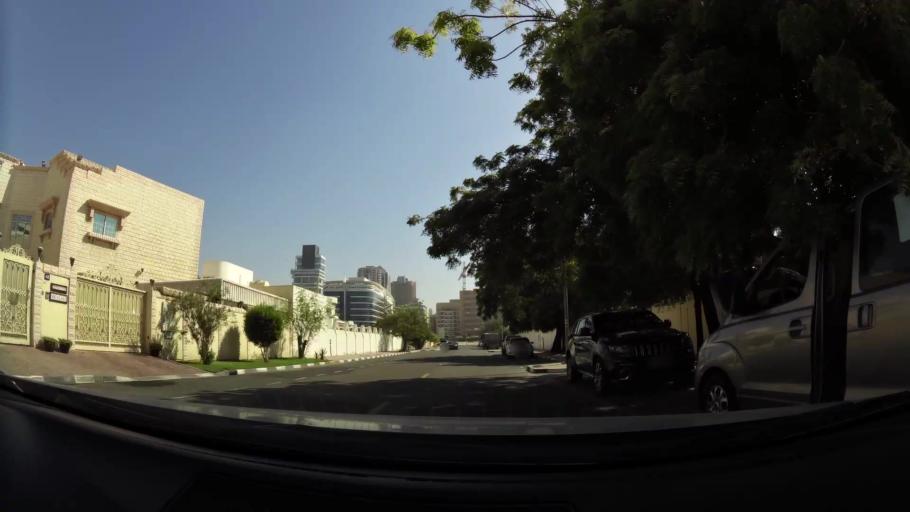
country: AE
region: Ash Shariqah
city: Sharjah
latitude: 25.2481
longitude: 55.2916
